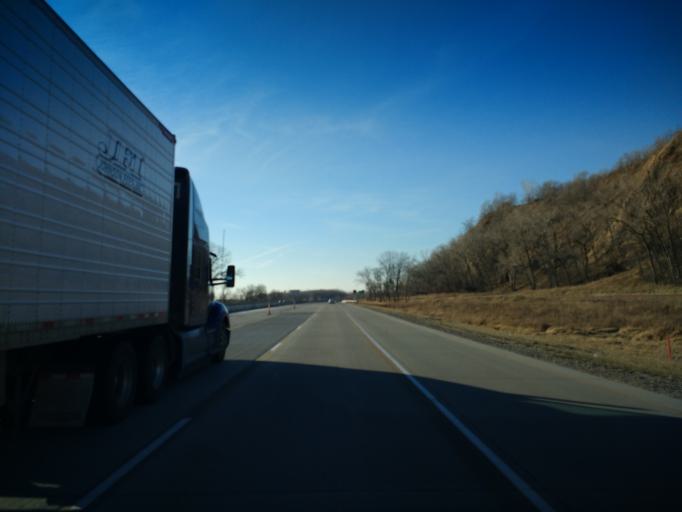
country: US
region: Nebraska
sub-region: Dakota County
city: South Sioux City
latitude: 42.4917
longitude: -96.4372
